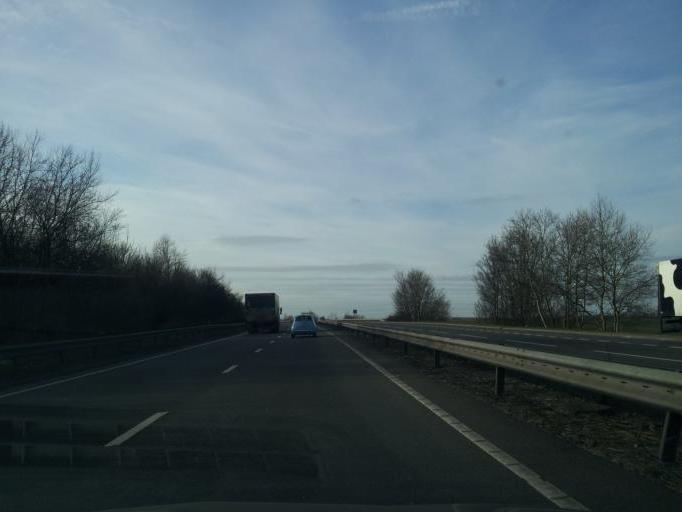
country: GB
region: England
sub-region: Cambridgeshire
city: Eaton Socon
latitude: 52.2310
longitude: -0.2905
